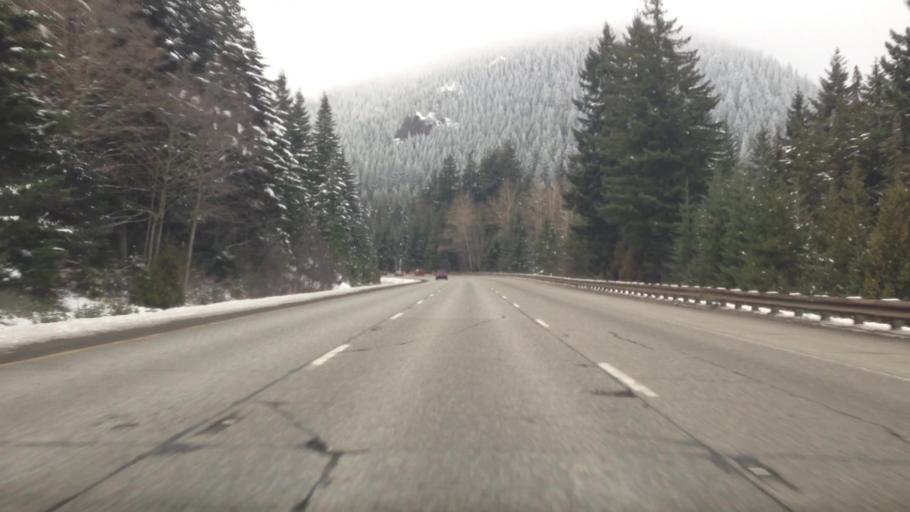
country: US
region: Washington
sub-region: Kittitas County
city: Cle Elum
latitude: 47.2687
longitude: -121.2288
